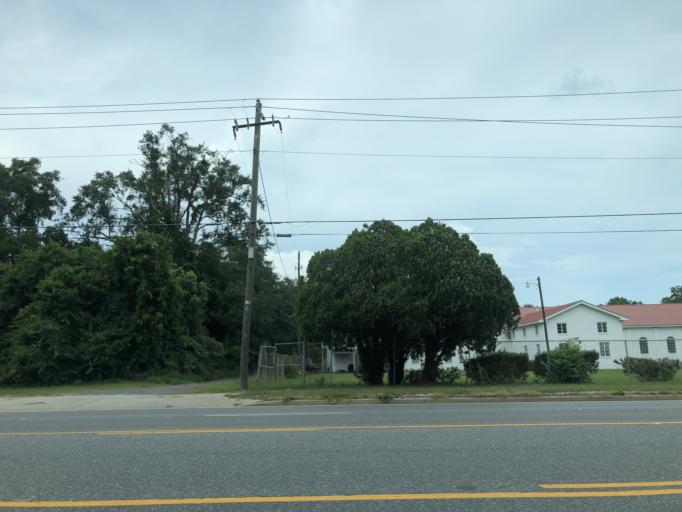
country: US
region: Georgia
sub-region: Wayne County
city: Jesup
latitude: 31.6033
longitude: -81.8760
